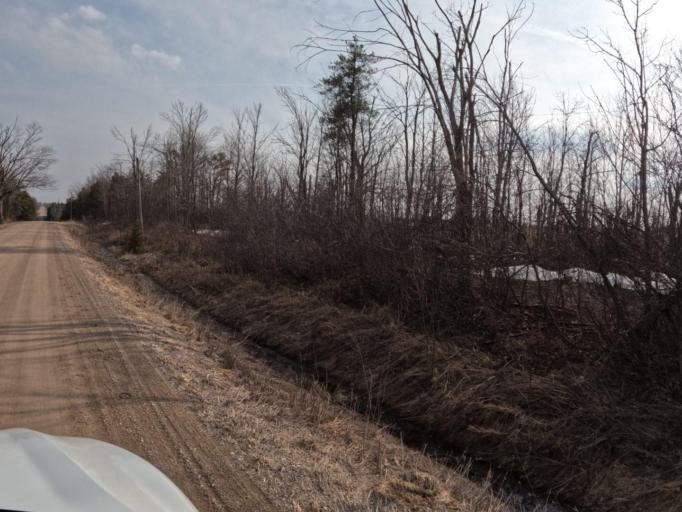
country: CA
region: Ontario
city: Orangeville
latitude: 43.9165
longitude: -80.2716
